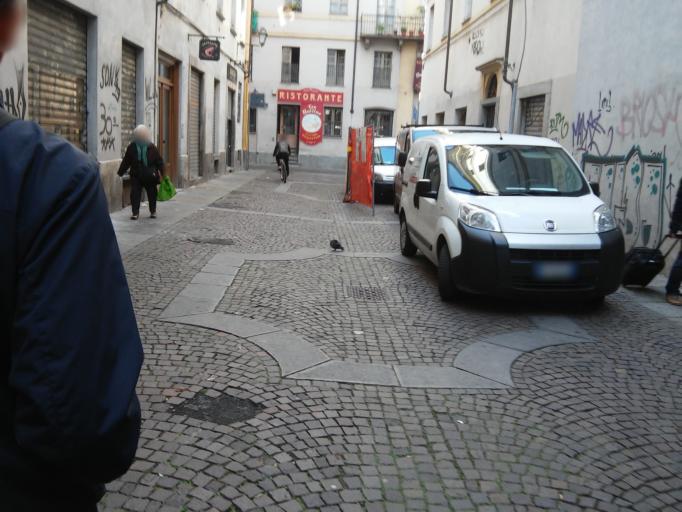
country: IT
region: Piedmont
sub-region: Provincia di Torino
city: Turin
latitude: 45.0759
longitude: 7.6822
